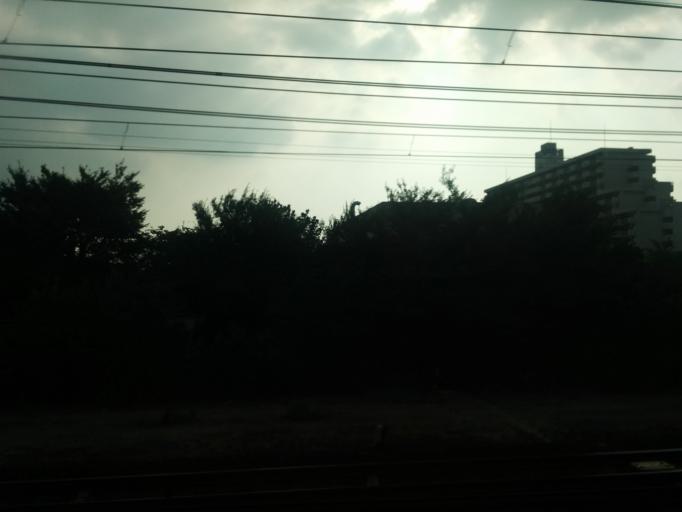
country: JP
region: Aichi
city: Obu
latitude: 35.0862
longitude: 136.9313
